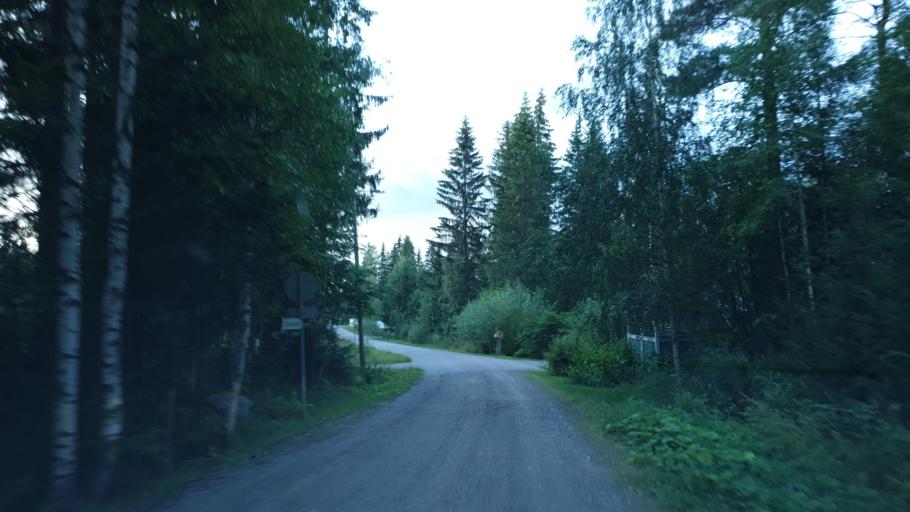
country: FI
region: Northern Savo
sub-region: Varkaus
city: Leppaevirta
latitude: 62.5817
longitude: 27.6233
